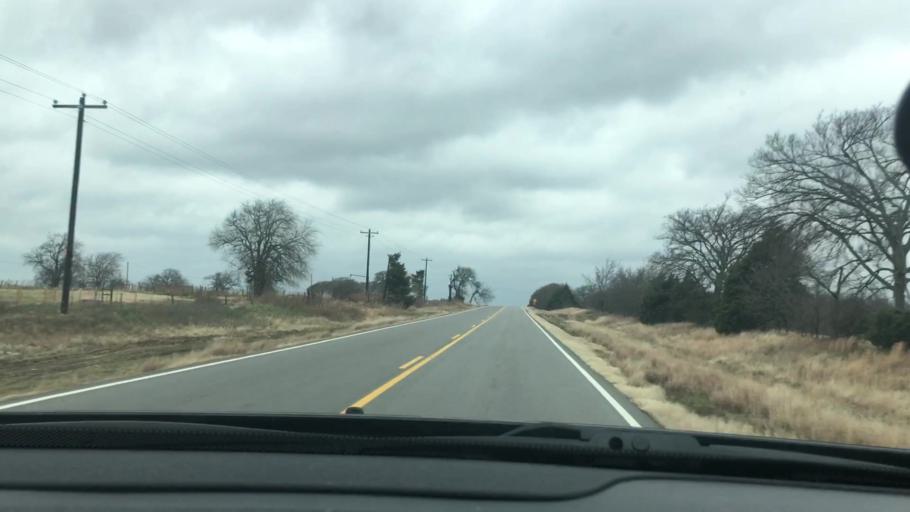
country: US
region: Oklahoma
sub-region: Atoka County
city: Atoka
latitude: 34.3749
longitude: -96.2453
